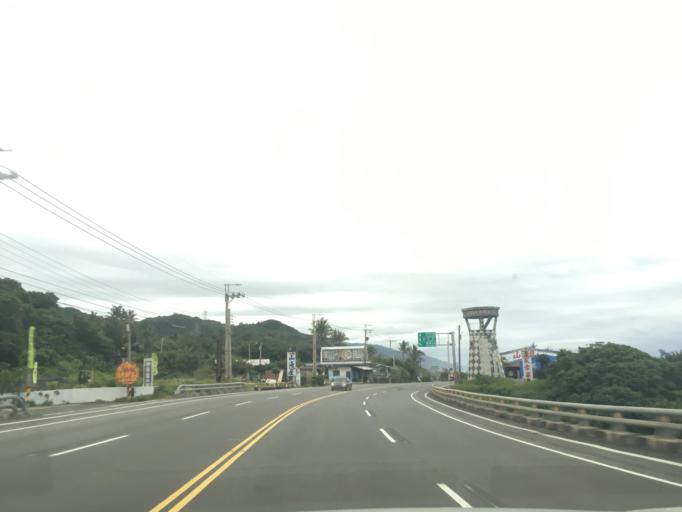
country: TW
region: Taiwan
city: Hengchun
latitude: 22.3028
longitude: 120.8889
